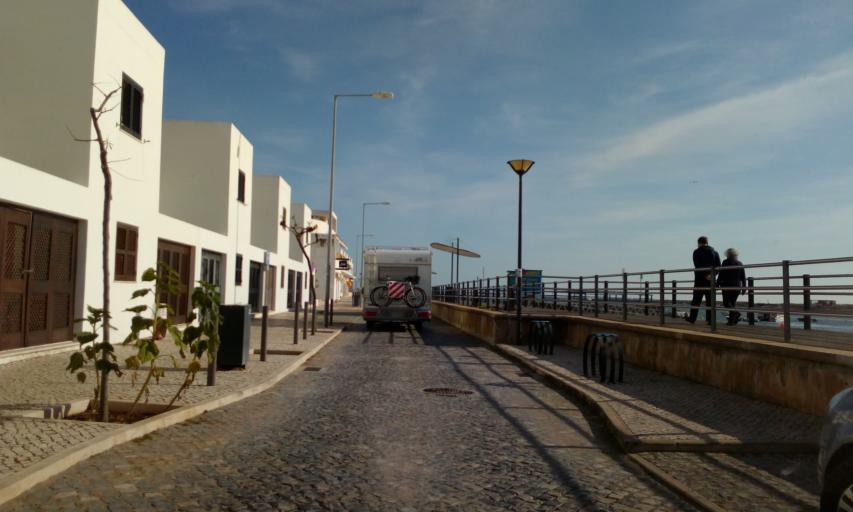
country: PT
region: Faro
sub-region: Tavira
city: Tavira
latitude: 37.1357
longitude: -7.5981
